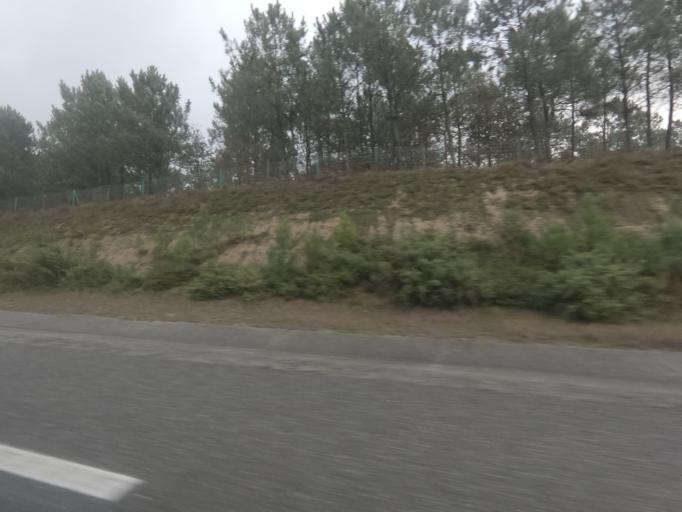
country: ES
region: Galicia
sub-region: Provincia de Pontevedra
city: Porrino
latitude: 42.1956
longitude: -8.6638
